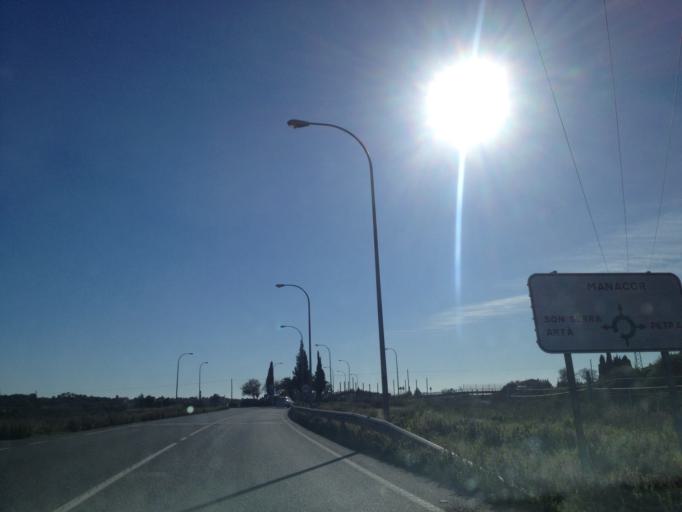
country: ES
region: Balearic Islands
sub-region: Illes Balears
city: Petra
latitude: 39.6180
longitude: 3.1207
